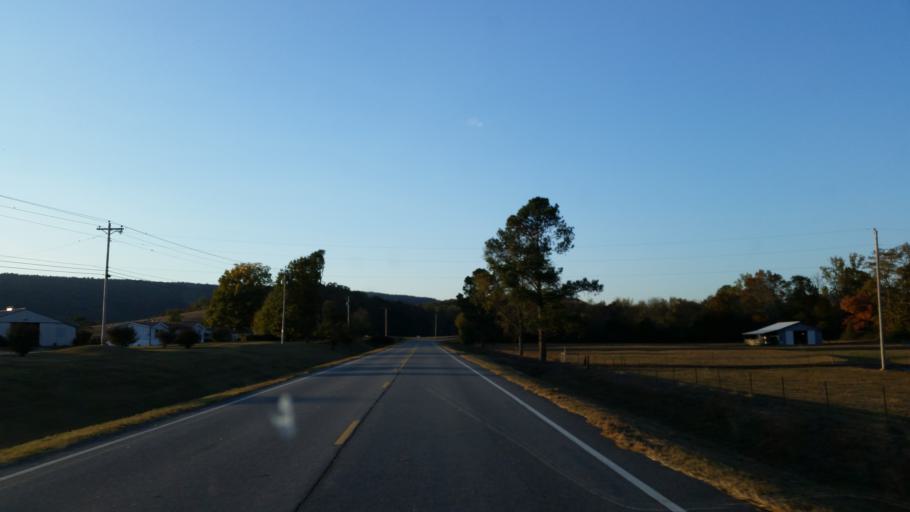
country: US
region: Georgia
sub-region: Gordon County
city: Calhoun
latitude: 34.5881
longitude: -85.0348
